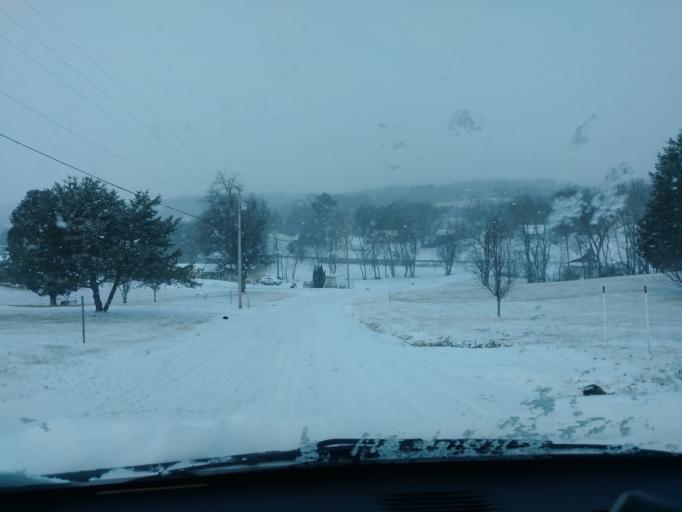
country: US
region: Tennessee
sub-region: Greene County
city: Mosheim
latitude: 36.0990
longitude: -82.9259
